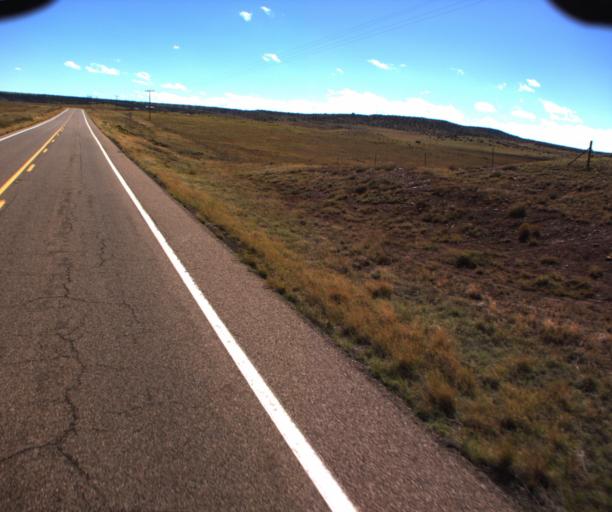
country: US
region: Arizona
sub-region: Apache County
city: Saint Johns
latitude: 34.4879
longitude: -109.6201
